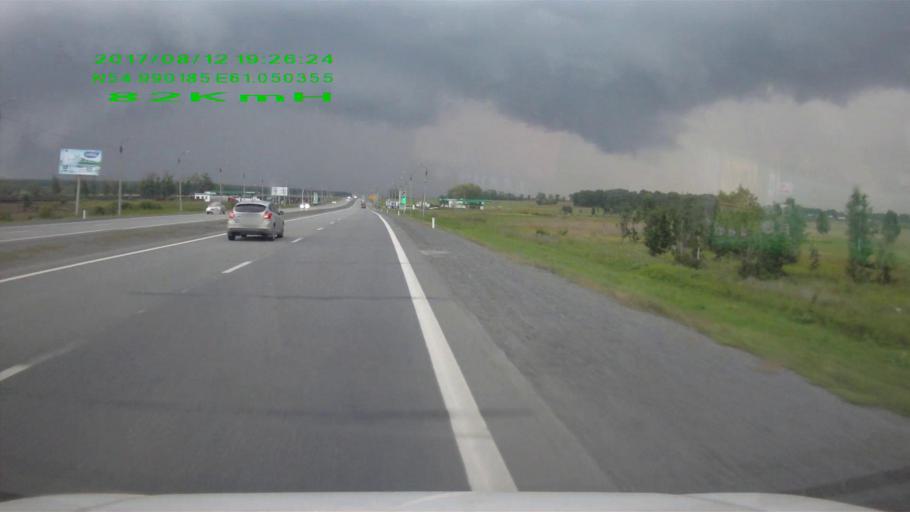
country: RU
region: Chelyabinsk
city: Poletayevo
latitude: 54.9895
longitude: 61.0472
